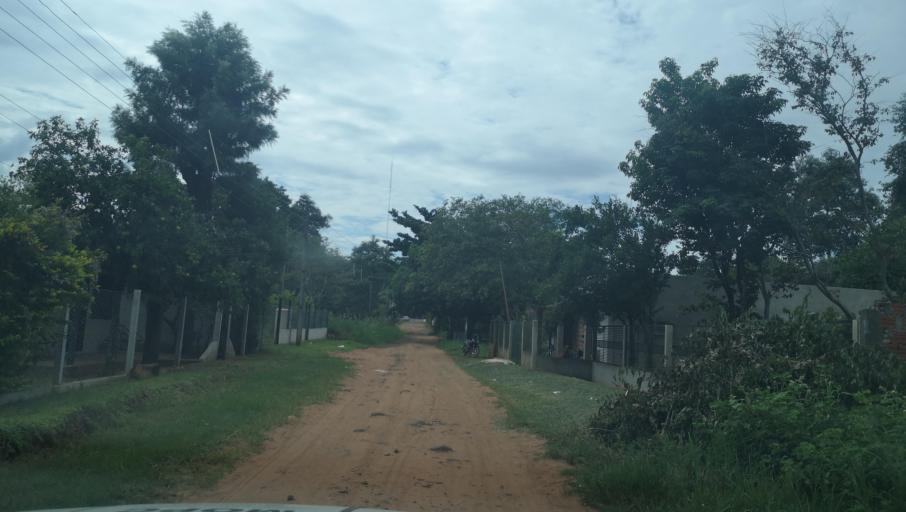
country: PY
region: San Pedro
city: Capiibary
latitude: -24.7261
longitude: -56.0205
